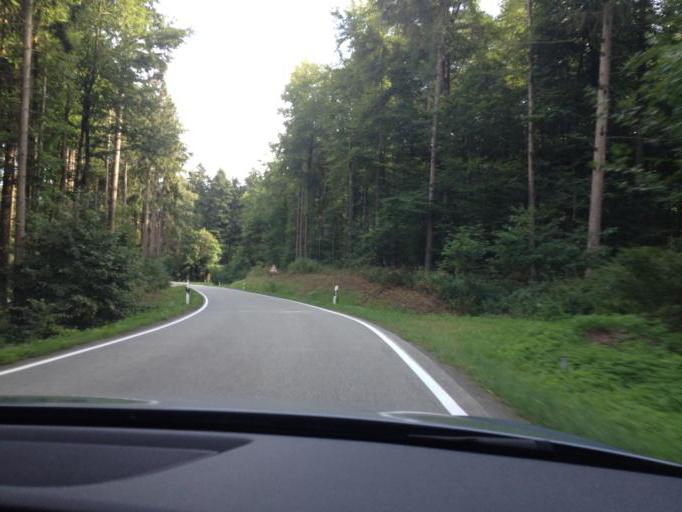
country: DE
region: Rheinland-Pfalz
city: Dunzweiler
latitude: 49.4070
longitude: 7.2969
